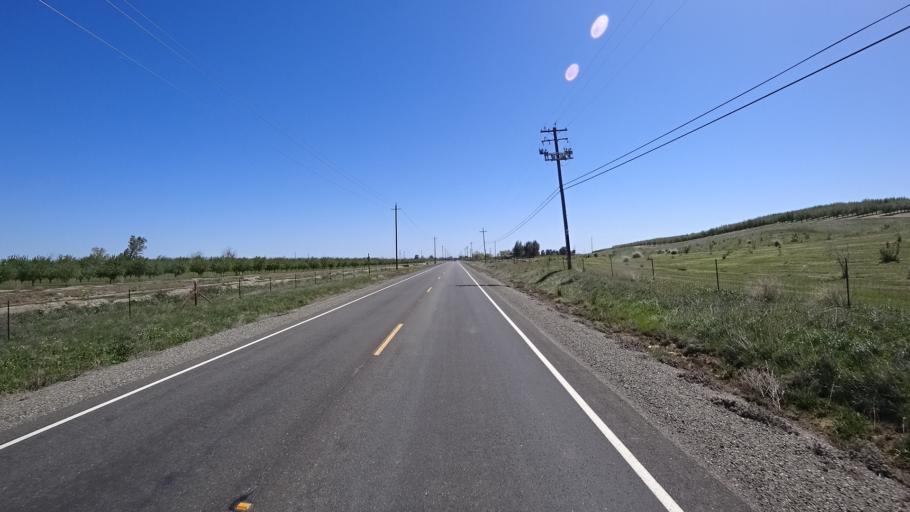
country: US
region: California
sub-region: Glenn County
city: Orland
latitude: 39.7801
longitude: -122.2892
